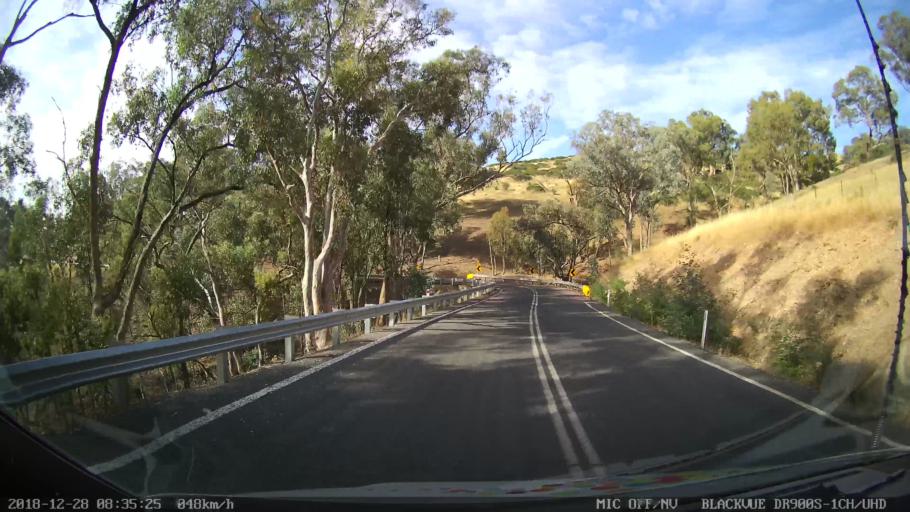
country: AU
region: New South Wales
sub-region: Blayney
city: Blayney
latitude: -33.9832
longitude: 149.3100
